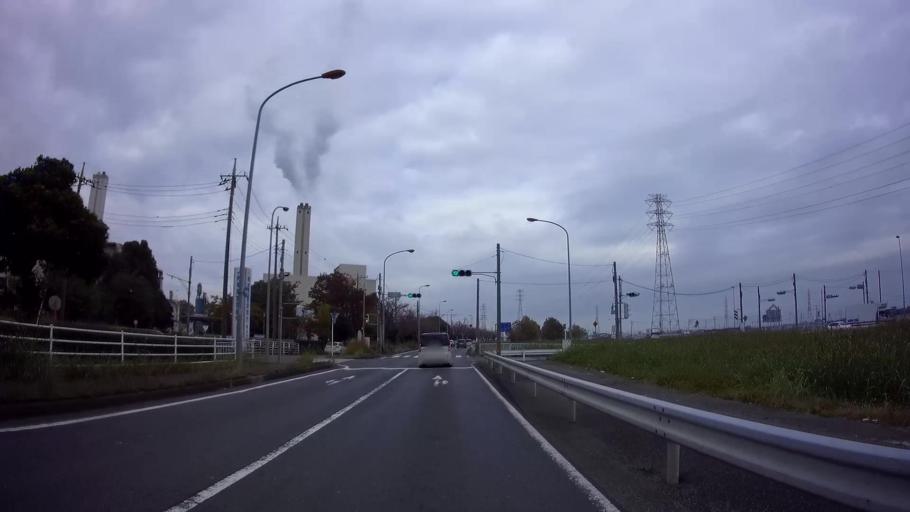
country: JP
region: Saitama
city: Menuma
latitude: 36.1957
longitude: 139.3405
